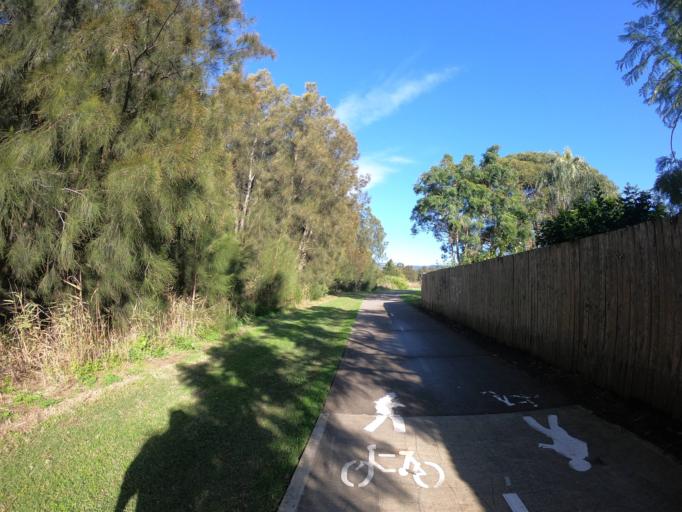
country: AU
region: New South Wales
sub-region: Wollongong
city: East Corrimal
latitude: -34.3707
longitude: 150.9225
